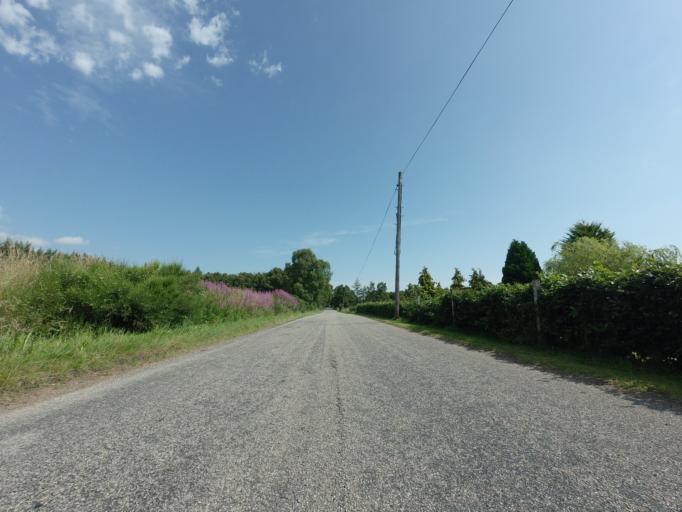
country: GB
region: Scotland
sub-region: Highland
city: Invergordon
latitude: 57.7294
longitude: -4.1936
